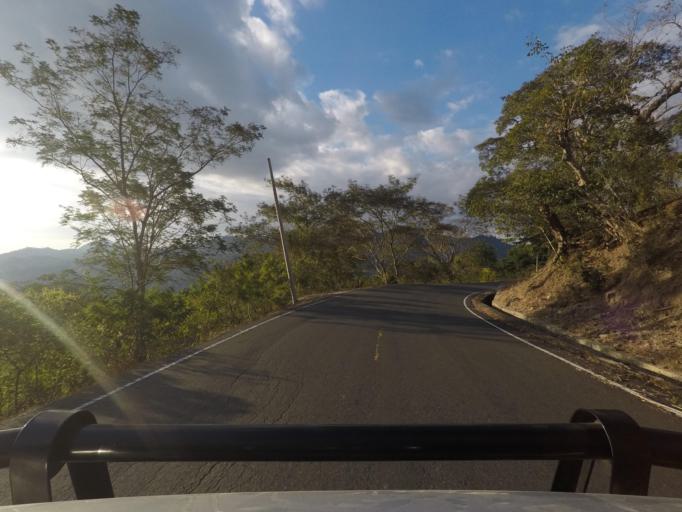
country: TL
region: Bobonaro
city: Maliana
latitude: -8.9520
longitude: 125.0881
